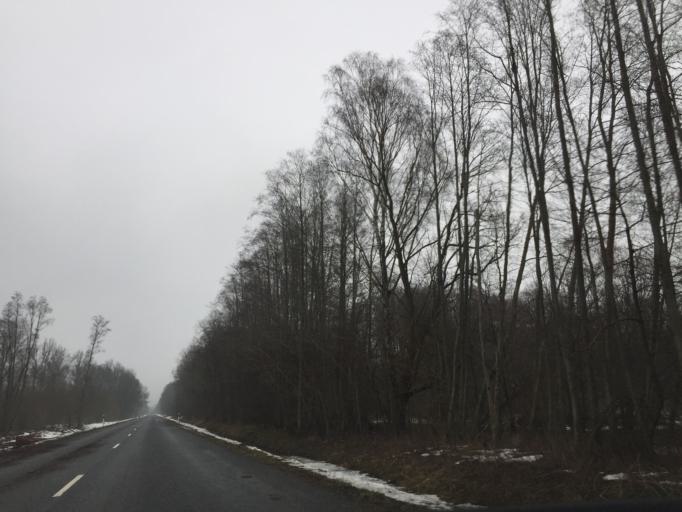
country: EE
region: Saare
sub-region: Kuressaare linn
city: Kuressaare
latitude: 58.3462
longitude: 22.7933
